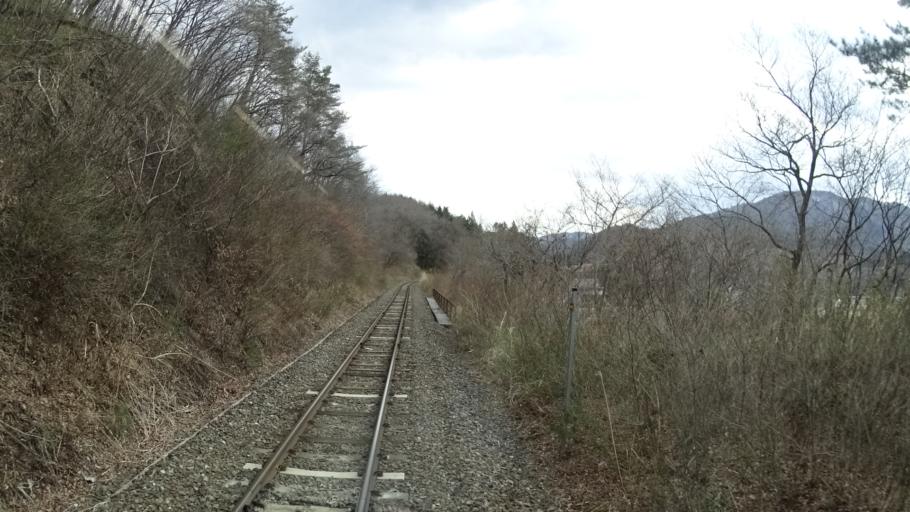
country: JP
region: Iwate
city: Tono
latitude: 39.3092
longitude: 141.3796
